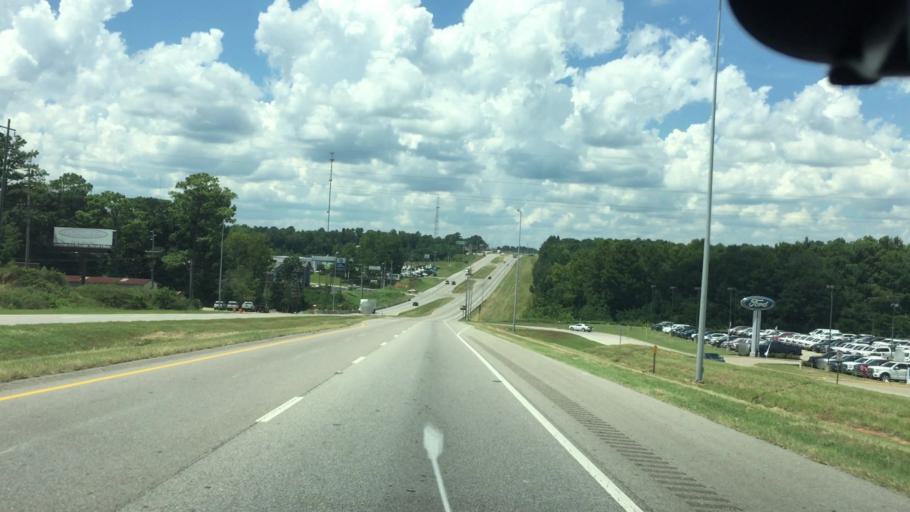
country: US
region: Alabama
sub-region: Pike County
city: Troy
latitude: 31.7957
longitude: -85.9804
